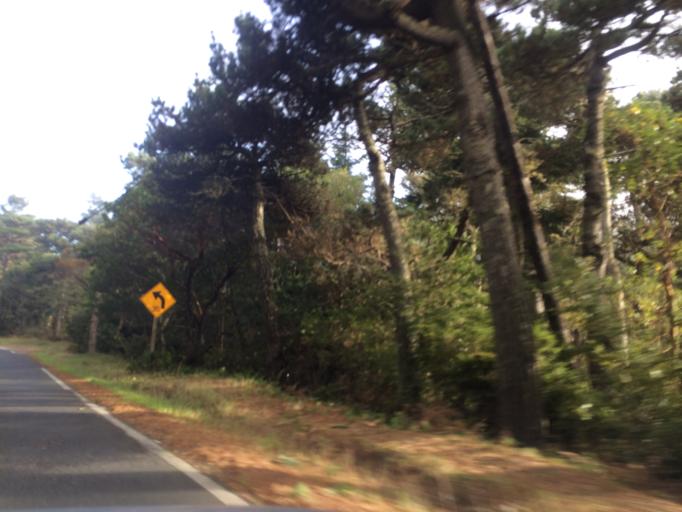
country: US
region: California
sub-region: Marin County
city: Inverness
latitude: 38.1078
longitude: -122.8803
